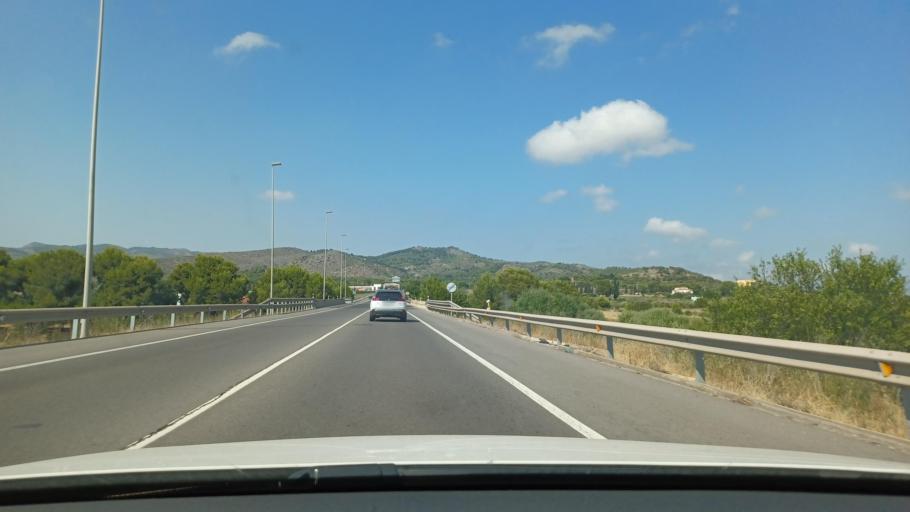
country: ES
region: Valencia
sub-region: Provincia de Castello
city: Borriol
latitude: 39.9967
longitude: -0.0879
